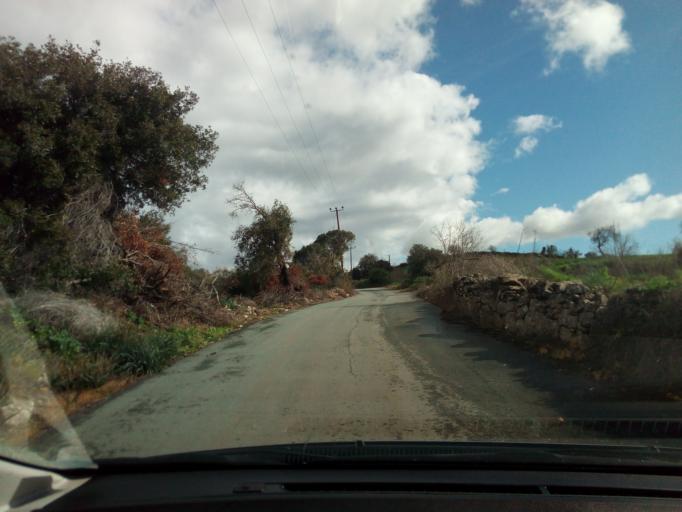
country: CY
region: Pafos
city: Tala
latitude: 34.9205
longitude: 32.5091
